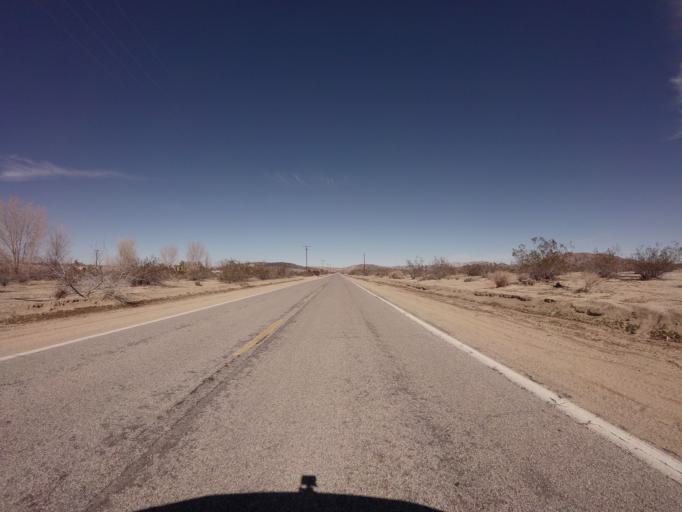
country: US
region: California
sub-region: San Bernardino County
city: Yucca Valley
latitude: 34.2673
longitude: -116.4045
